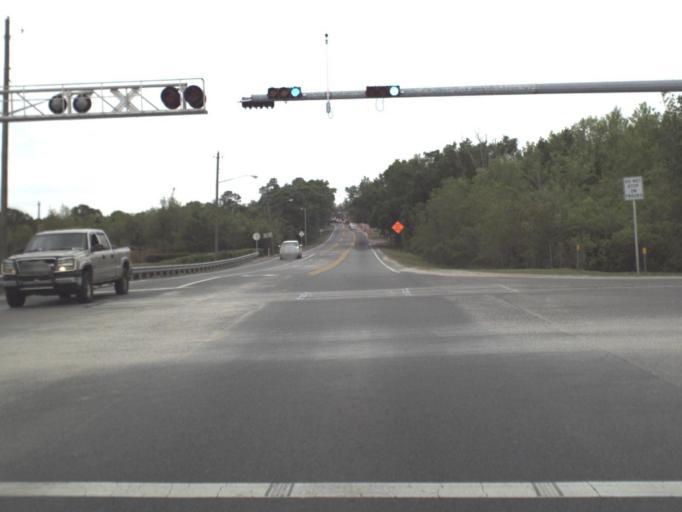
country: US
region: Florida
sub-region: Escambia County
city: Ferry Pass
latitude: 30.5135
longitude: -87.1647
